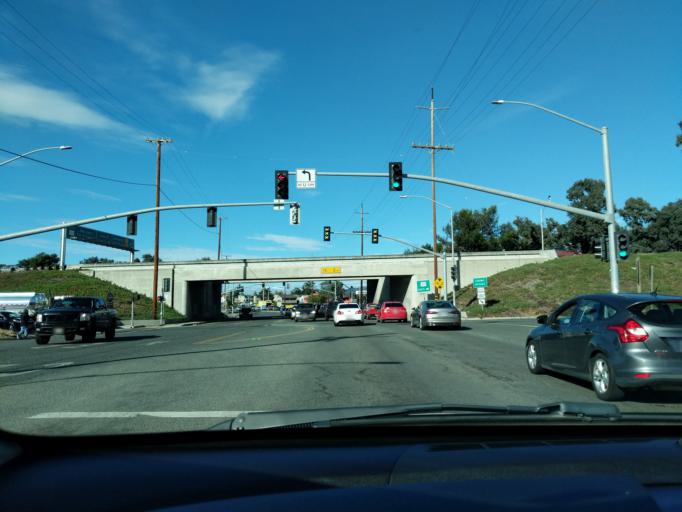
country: US
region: California
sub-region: Monterey County
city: Salinas
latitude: 36.6660
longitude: -121.6285
